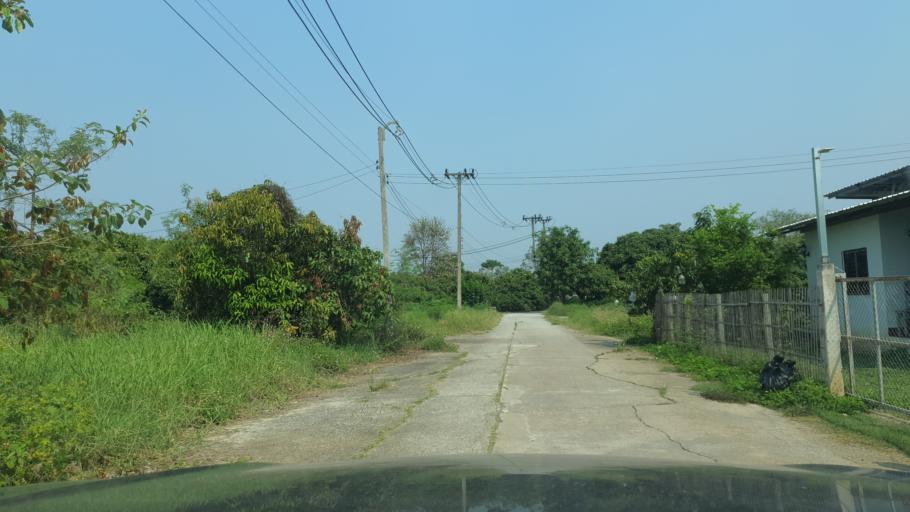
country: TH
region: Chiang Mai
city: Saraphi
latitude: 18.6688
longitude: 98.9912
